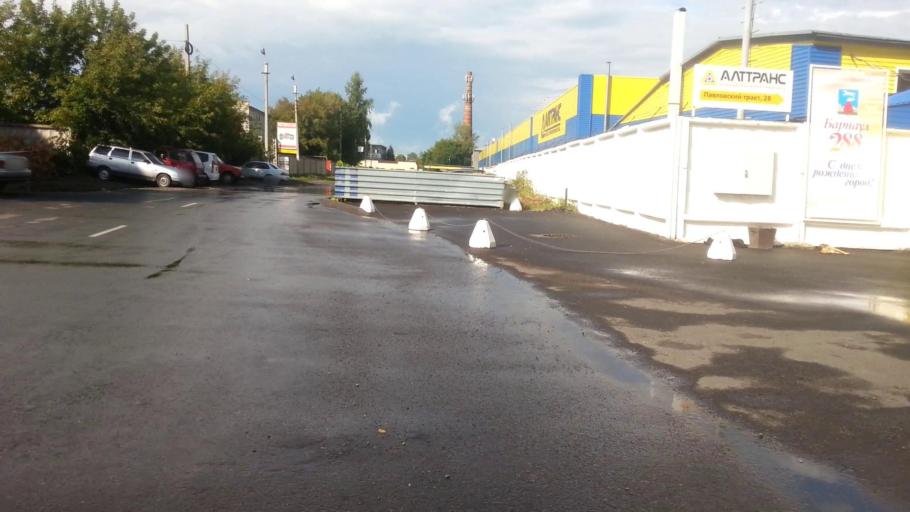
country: RU
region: Altai Krai
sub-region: Gorod Barnaulskiy
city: Barnaul
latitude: 53.3422
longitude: 83.7228
